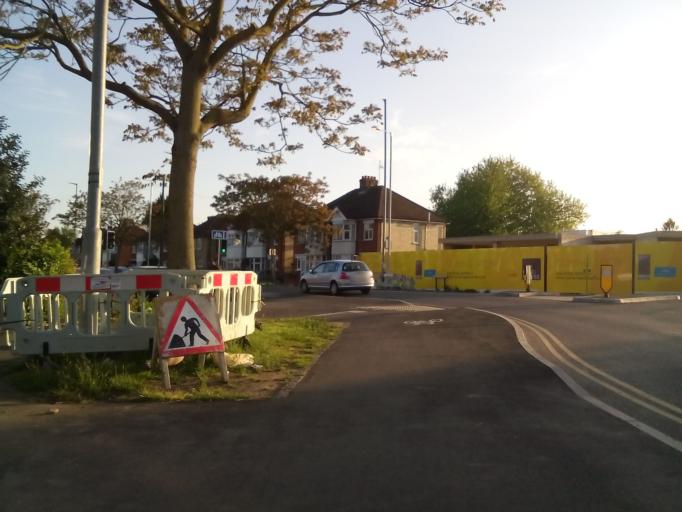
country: GB
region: England
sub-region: Cambridgeshire
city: Cambridge
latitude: 52.1918
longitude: 0.1548
